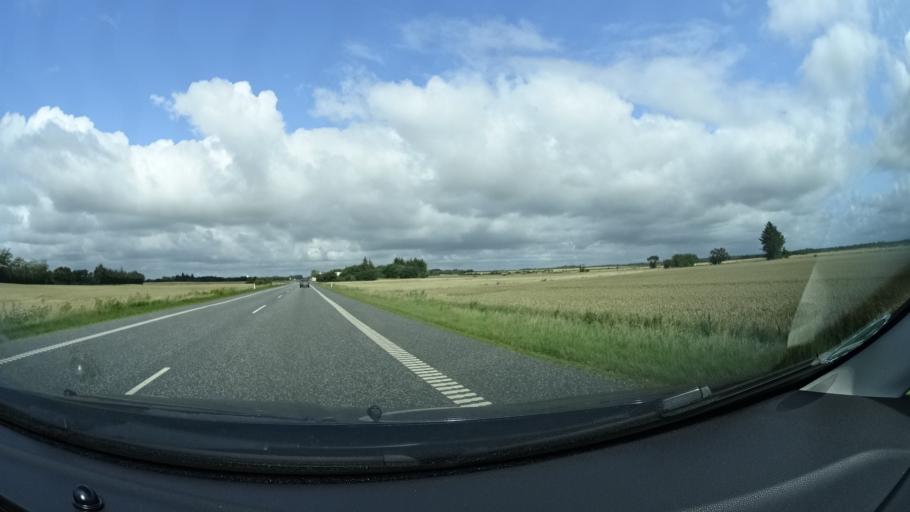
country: DK
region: Central Jutland
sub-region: Holstebro Kommune
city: Ulfborg
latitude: 56.2861
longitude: 8.3337
